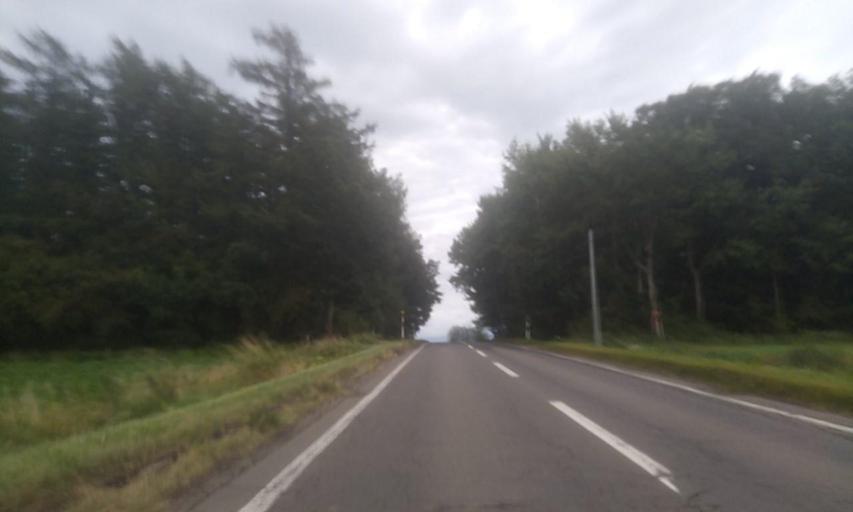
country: JP
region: Hokkaido
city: Abashiri
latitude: 43.8948
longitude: 144.5309
